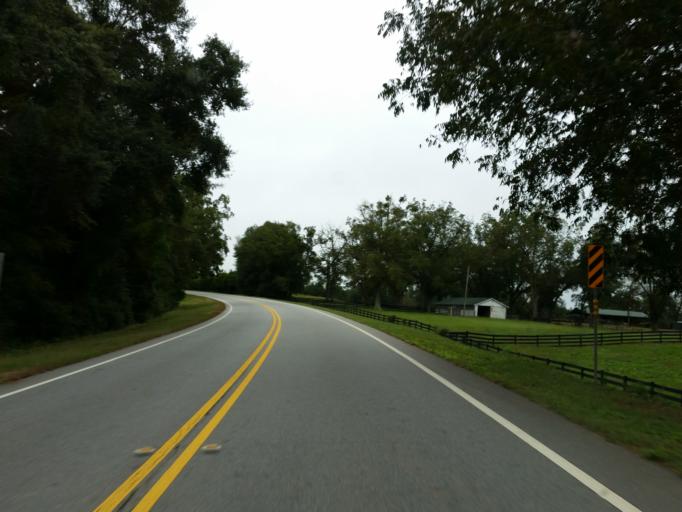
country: US
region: Georgia
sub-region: Lamar County
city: Barnesville
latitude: 32.9571
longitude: -84.1094
